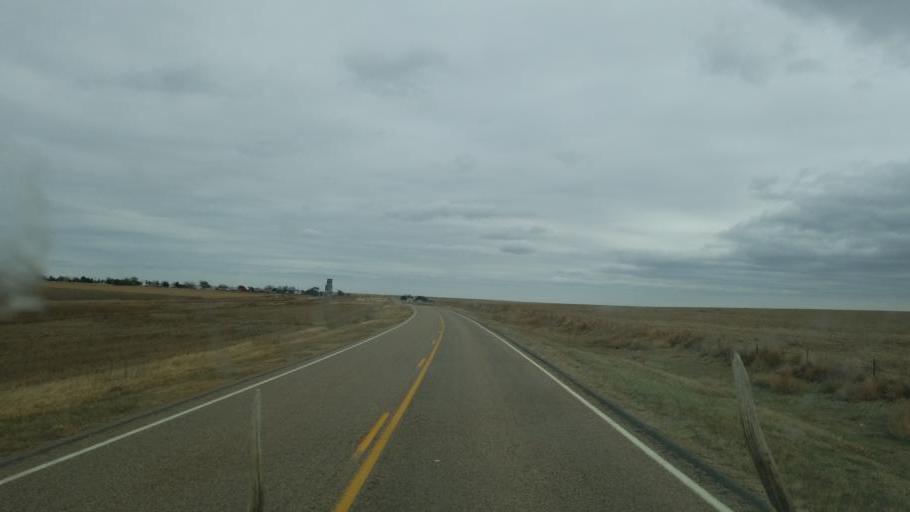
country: US
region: Colorado
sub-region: Cheyenne County
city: Cheyenne Wells
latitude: 38.8504
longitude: -102.1908
